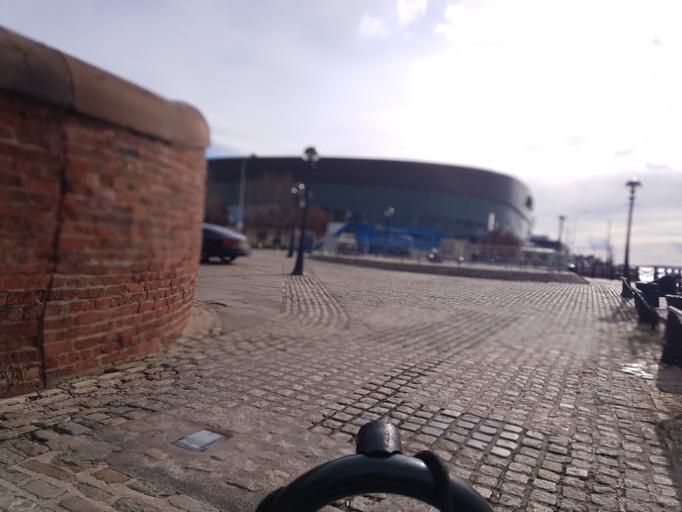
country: GB
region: England
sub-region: Liverpool
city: Liverpool
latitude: 53.3988
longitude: -2.9934
